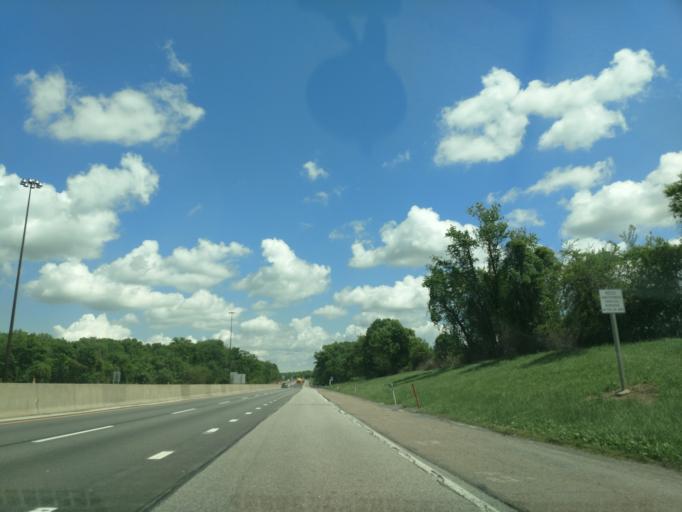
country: US
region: Pennsylvania
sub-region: Chester County
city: Chester Springs
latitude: 40.0670
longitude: -75.6635
